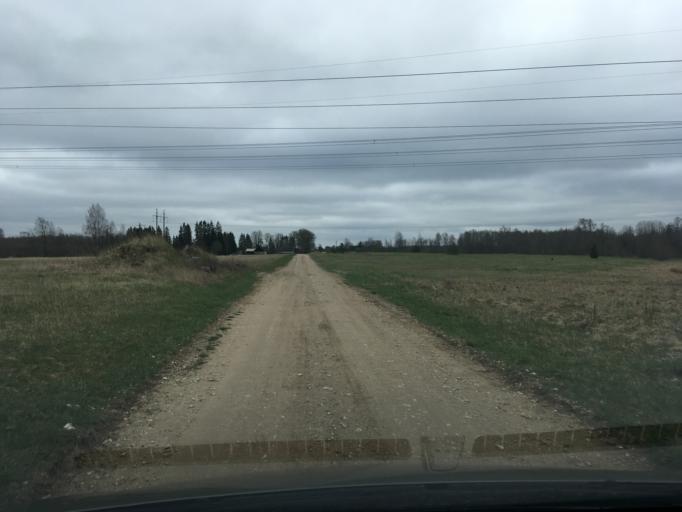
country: EE
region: Harju
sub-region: Raasiku vald
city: Arukula
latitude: 59.2732
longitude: 25.1174
